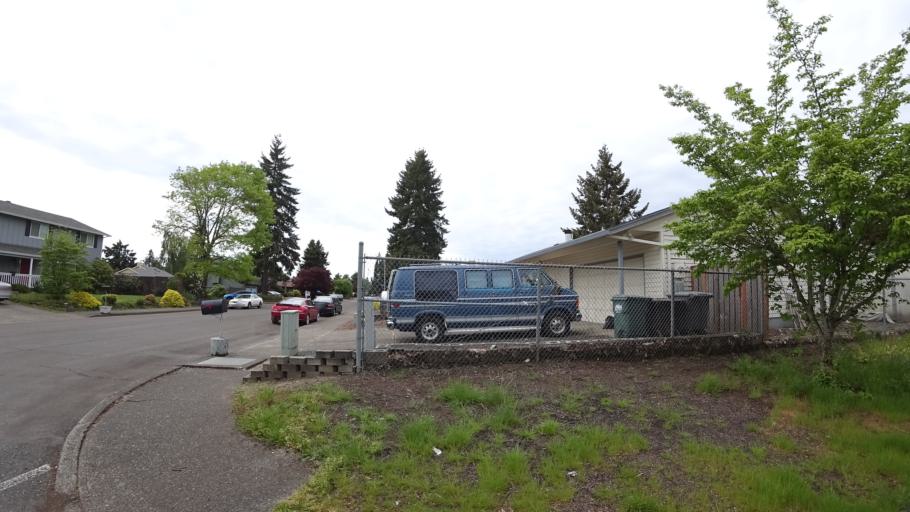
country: US
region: Oregon
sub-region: Washington County
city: Hillsboro
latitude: 45.4973
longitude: -122.9645
